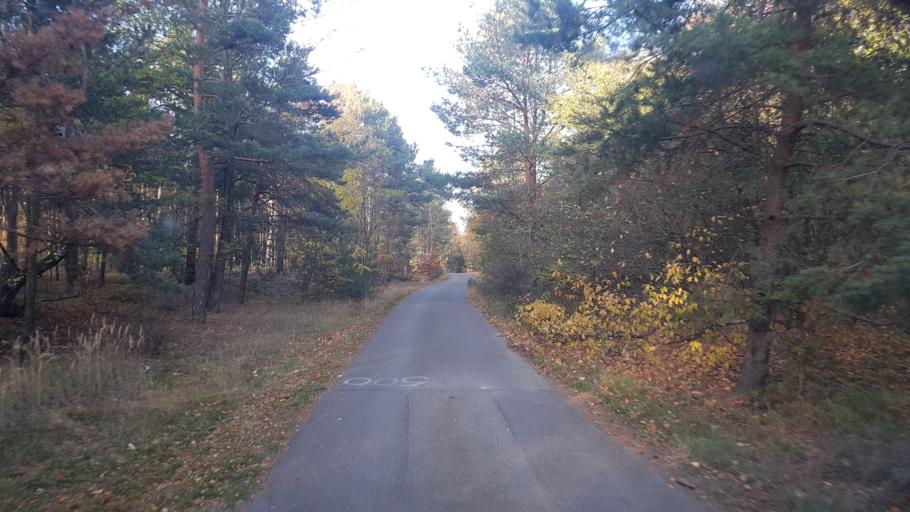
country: DE
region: Brandenburg
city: Calau
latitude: 51.7092
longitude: 13.9491
